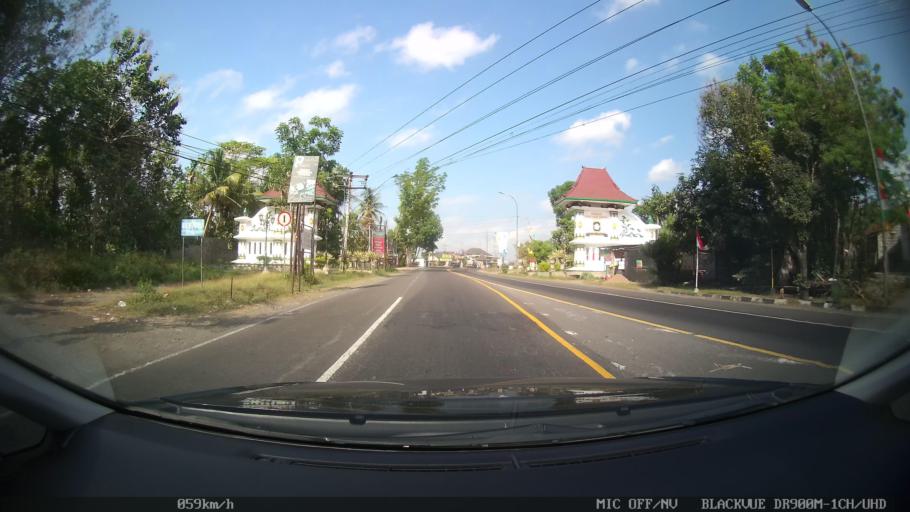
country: ID
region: Daerah Istimewa Yogyakarta
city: Godean
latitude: -7.8235
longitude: 110.2317
